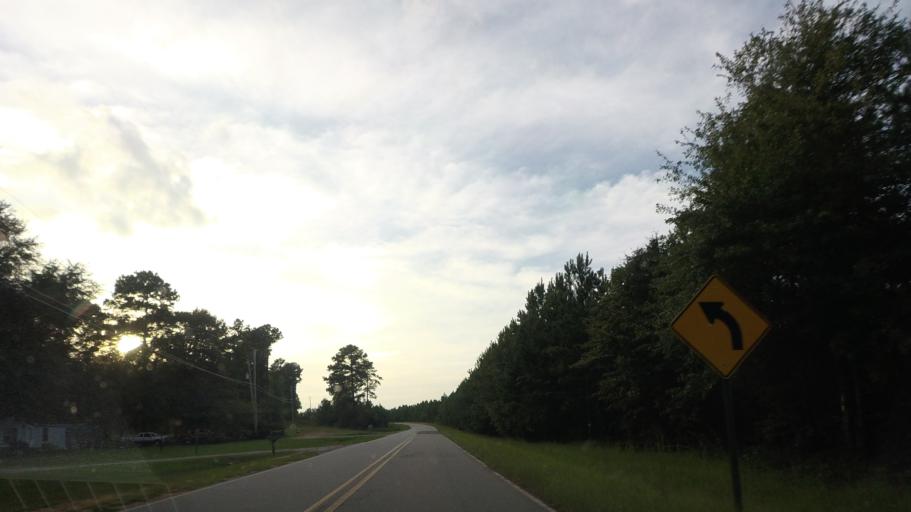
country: US
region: Georgia
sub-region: Bibb County
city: Macon
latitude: 32.8768
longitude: -83.5167
